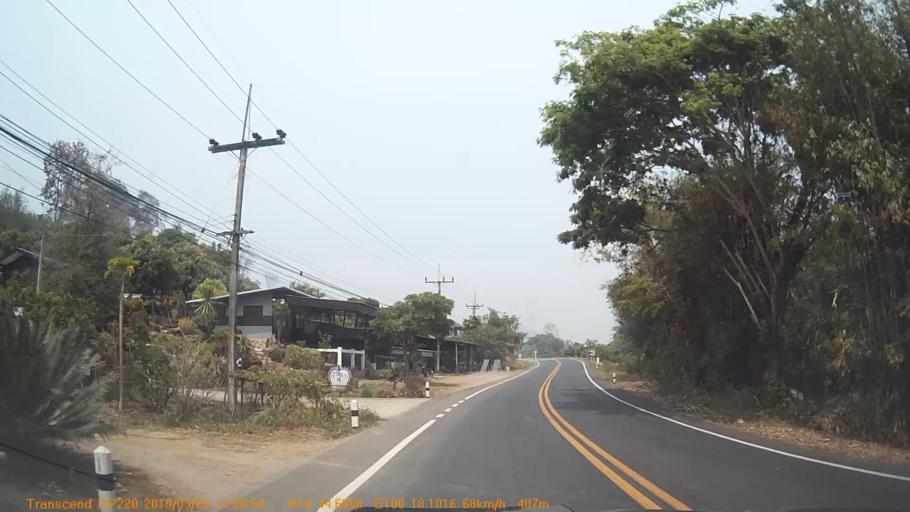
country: TH
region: Chiang Rai
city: Khun Tan
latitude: 19.7436
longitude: 100.3018
